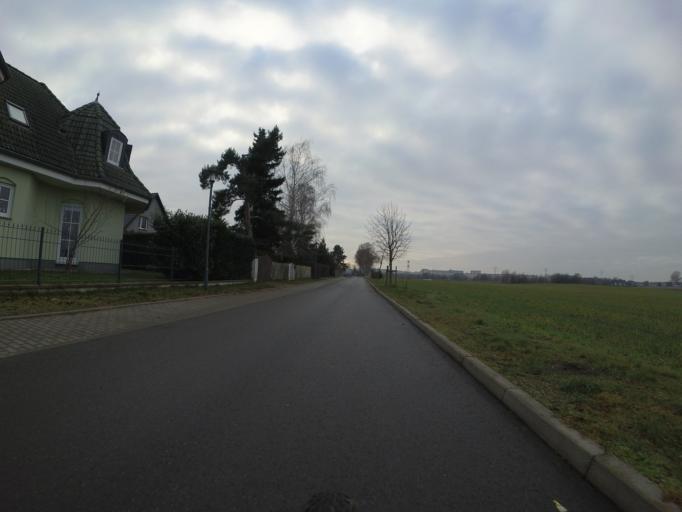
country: DE
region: Brandenburg
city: Ahrensfelde
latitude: 52.5725
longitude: 13.5928
